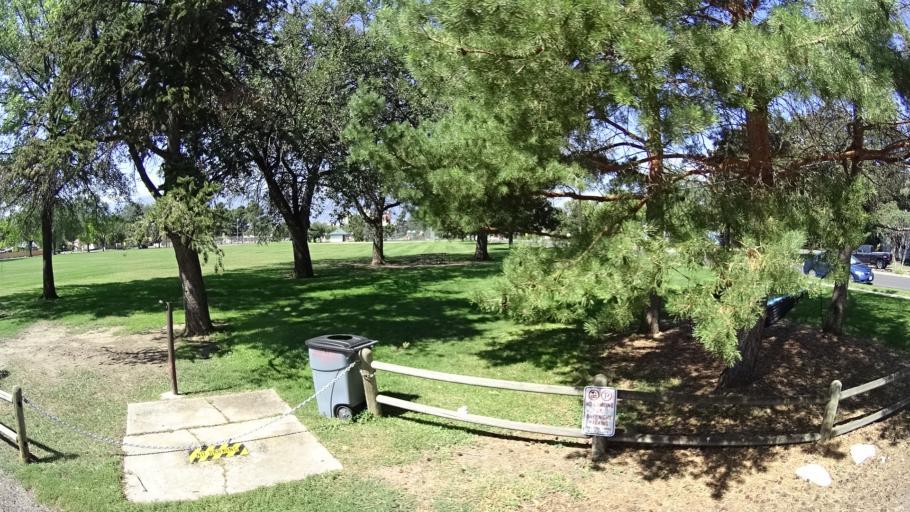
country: US
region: Colorado
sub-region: El Paso County
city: Colorado Springs
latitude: 38.8664
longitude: -104.8132
